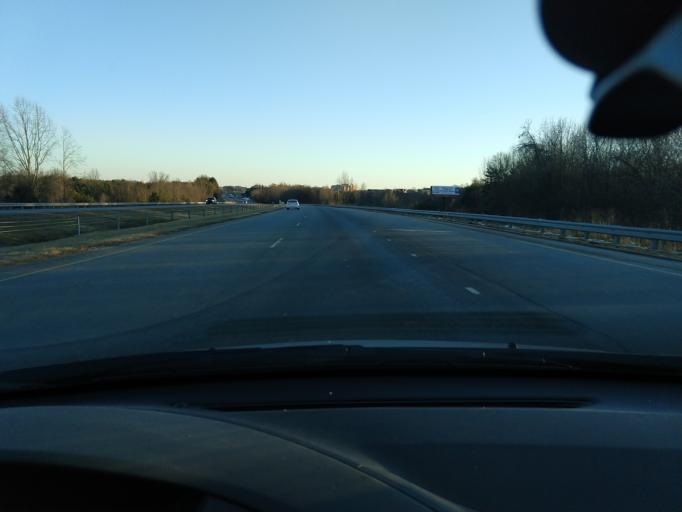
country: US
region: North Carolina
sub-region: Guilford County
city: Oak Ridge
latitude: 36.0930
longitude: -79.9662
